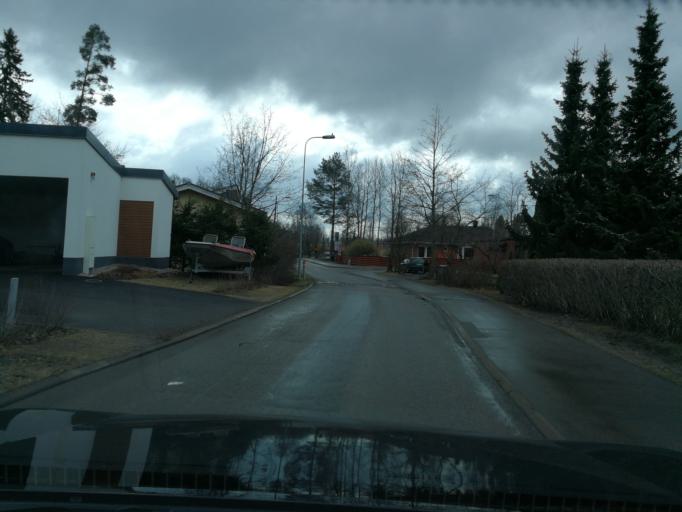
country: FI
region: Uusimaa
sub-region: Helsinki
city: Kauniainen
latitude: 60.1630
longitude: 24.6974
